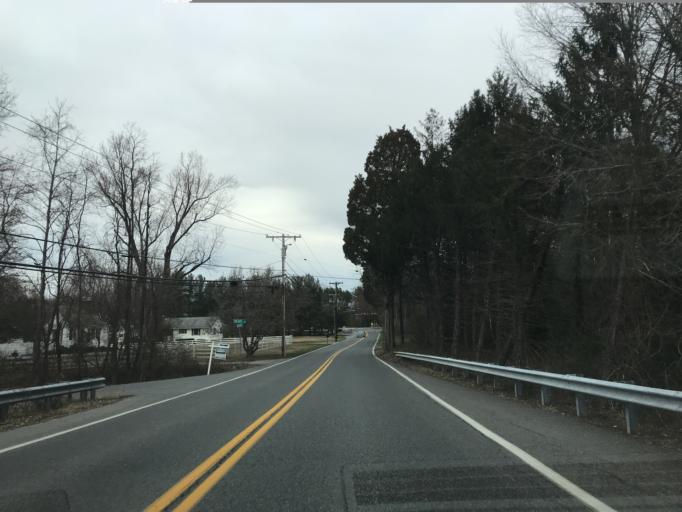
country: US
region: Maryland
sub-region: Anne Arundel County
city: Gambrills
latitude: 39.0579
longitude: -76.6300
